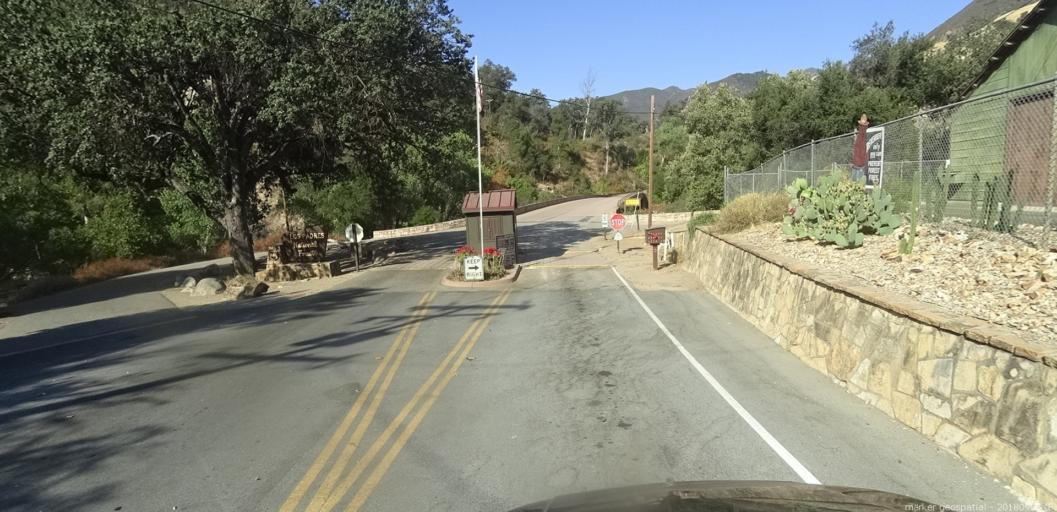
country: US
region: California
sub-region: Monterey County
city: Soledad
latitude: 36.2356
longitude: -121.4768
